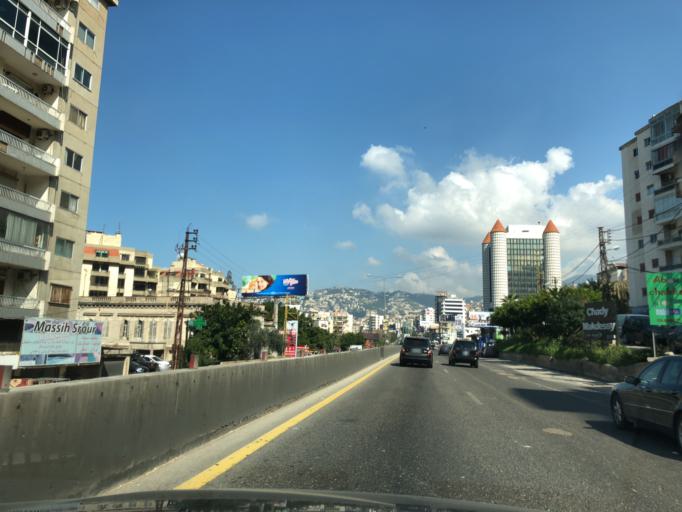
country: LB
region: Mont-Liban
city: Djounie
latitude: 33.9889
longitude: 35.6419
